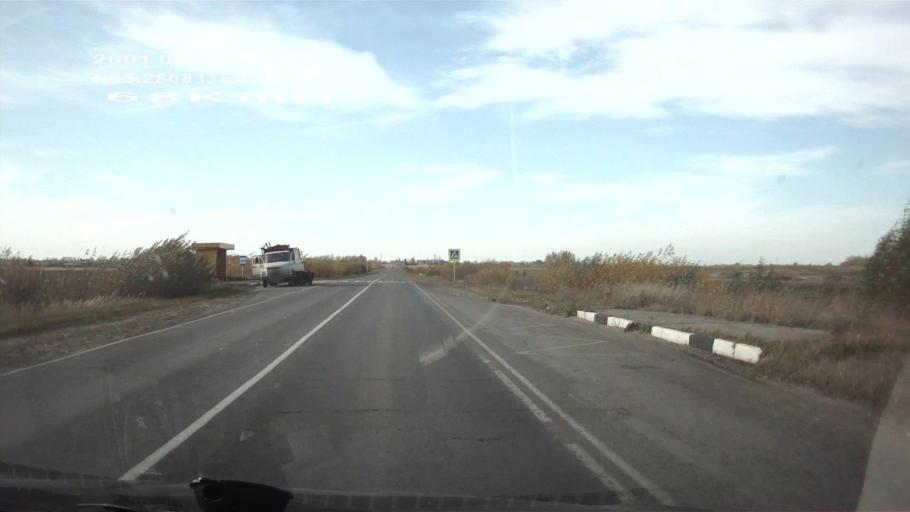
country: RU
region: Chuvashia
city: Ibresi
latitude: 55.2869
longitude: 47.0769
